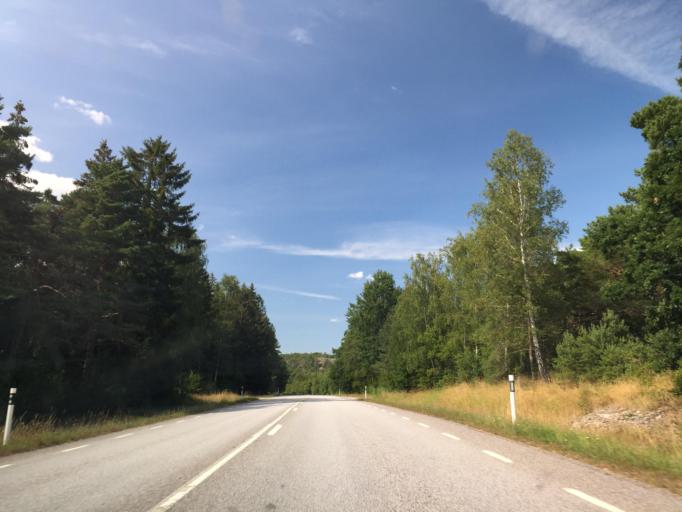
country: SE
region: Vaestra Goetaland
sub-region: Tanums Kommun
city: Tanumshede
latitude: 58.8185
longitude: 11.2622
